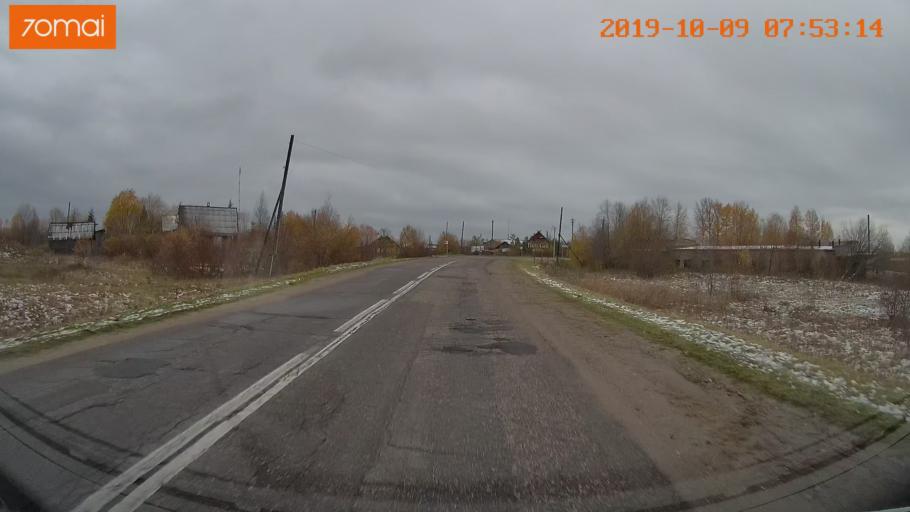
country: RU
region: Jaroslavl
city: Kukoboy
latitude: 58.6972
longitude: 39.8933
